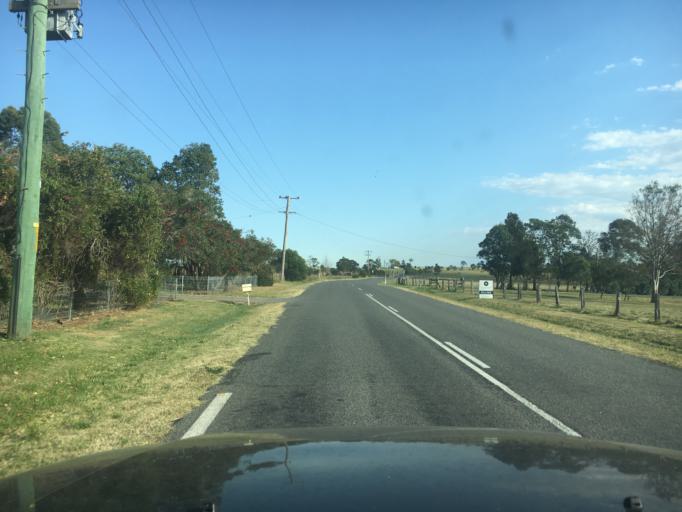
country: AU
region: New South Wales
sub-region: Cessnock
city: Branxton
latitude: -32.6011
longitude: 151.3360
